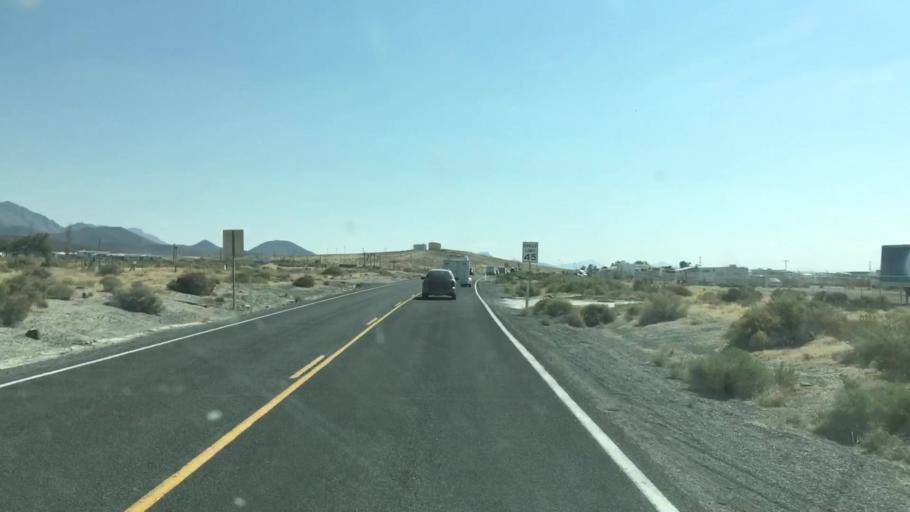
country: US
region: Nevada
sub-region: Pershing County
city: Lovelock
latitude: 40.5792
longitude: -119.3351
